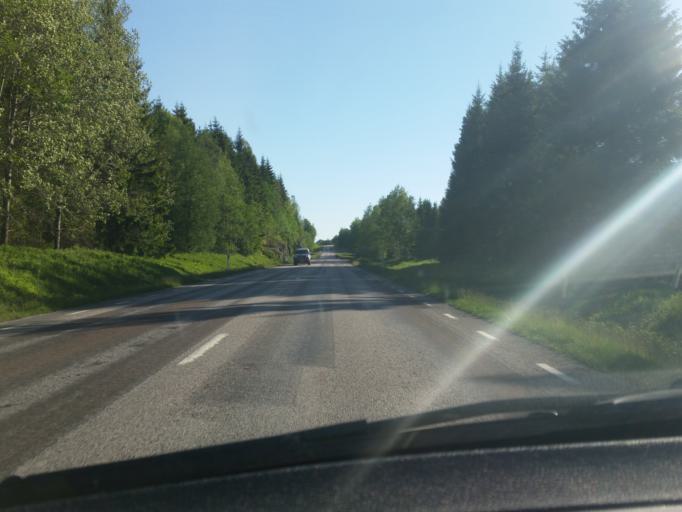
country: SE
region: Vaestra Goetaland
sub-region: Fargelanda Kommun
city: Faergelanda
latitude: 58.5802
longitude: 12.0184
